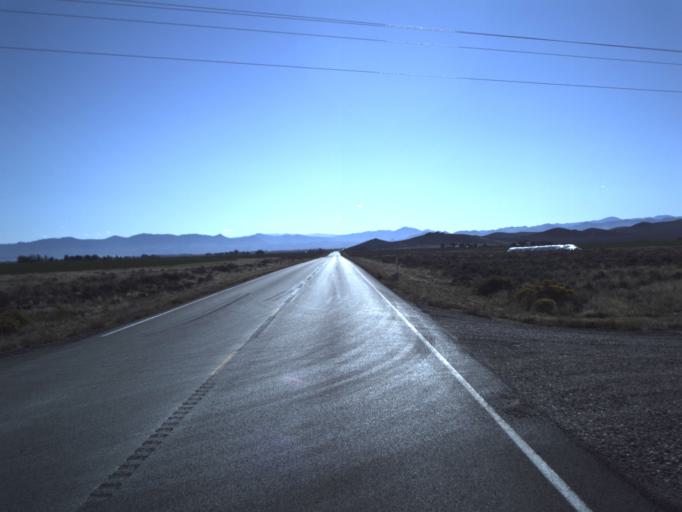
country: US
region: Utah
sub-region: Washington County
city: Enterprise
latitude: 37.7551
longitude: -113.7846
